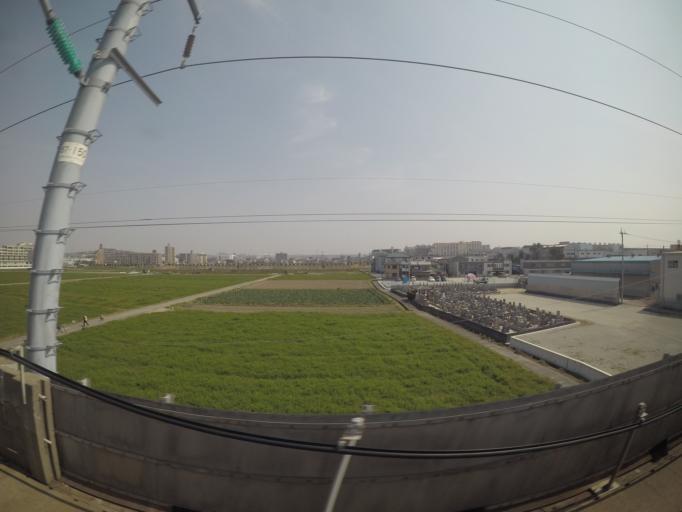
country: JP
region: Hyogo
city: Akashi
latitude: 34.6778
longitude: 134.9286
